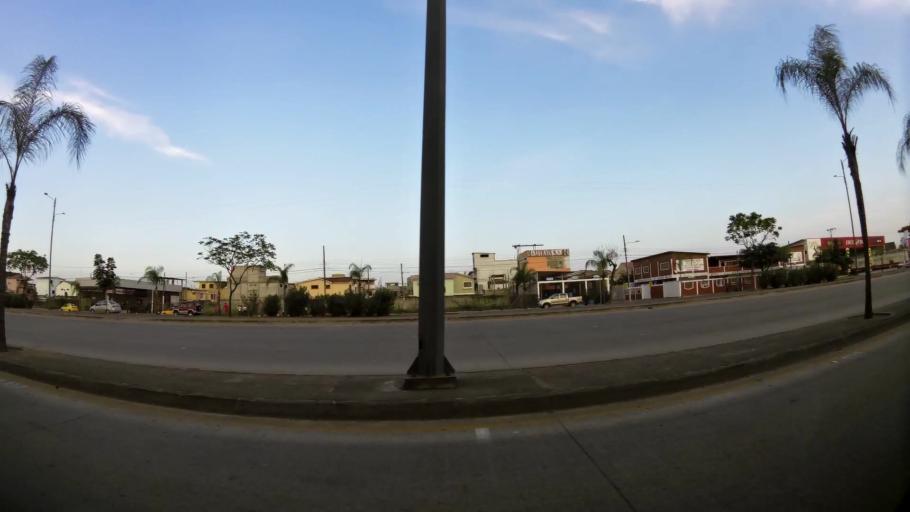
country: EC
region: Guayas
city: Eloy Alfaro
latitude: -2.1288
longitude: -79.8822
